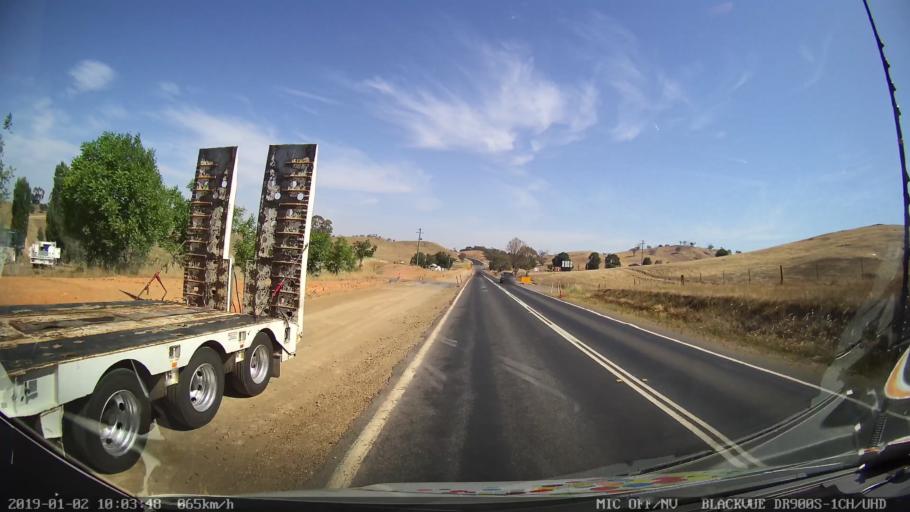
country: AU
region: New South Wales
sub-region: Gundagai
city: Gundagai
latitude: -35.1741
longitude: 148.1251
